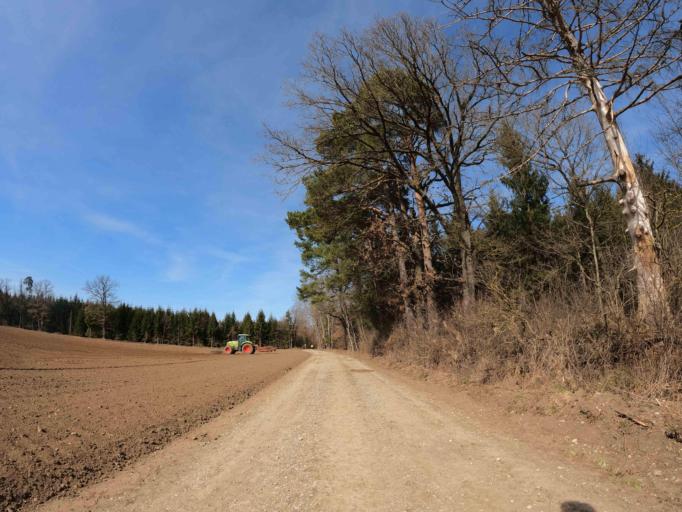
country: DE
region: Bavaria
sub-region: Upper Bavaria
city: Brunnthal
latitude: 47.9934
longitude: 11.7005
